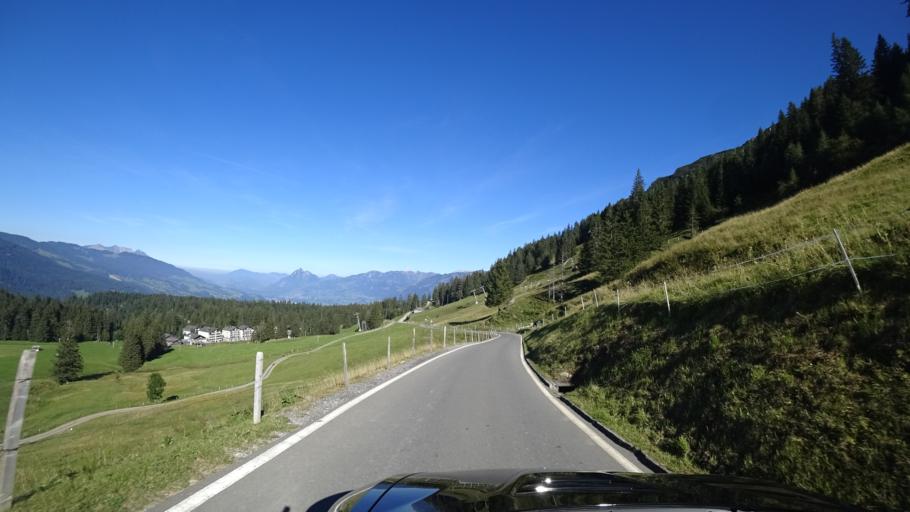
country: CH
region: Obwalden
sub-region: Obwalden
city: Lungern
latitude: 46.8225
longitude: 8.1047
